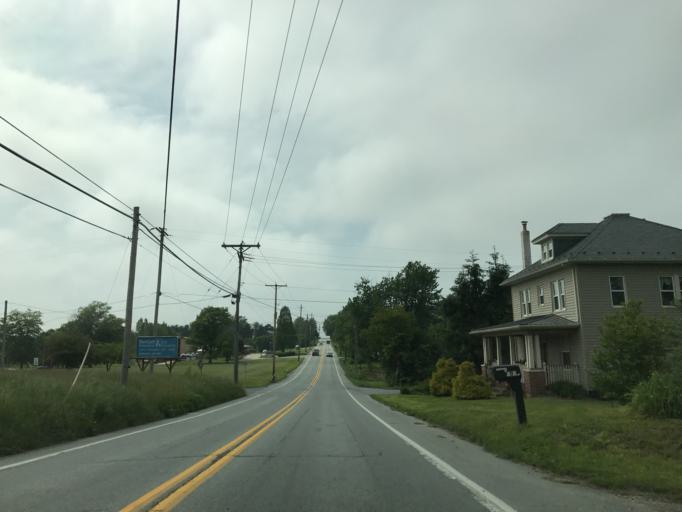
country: US
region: Pennsylvania
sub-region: York County
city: Windsor
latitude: 39.8951
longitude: -76.5643
